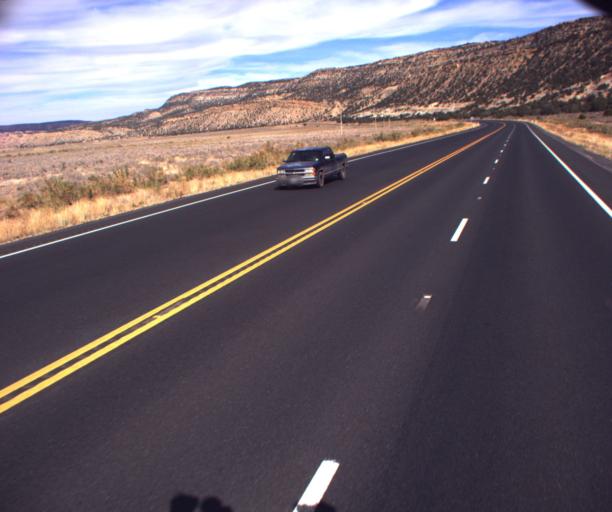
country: US
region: Arizona
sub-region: Navajo County
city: Kayenta
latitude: 36.5688
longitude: -110.4848
